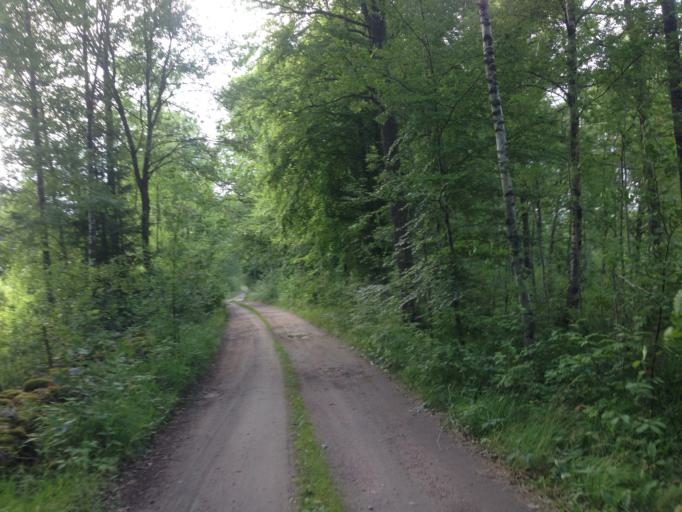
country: SE
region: Kronoberg
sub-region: Ljungby Kommun
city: Ljungby
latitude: 56.8661
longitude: 13.7926
